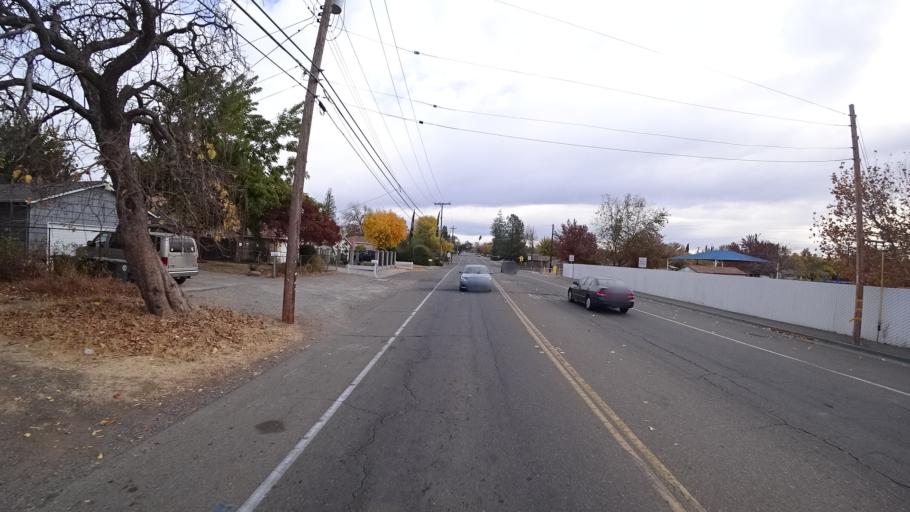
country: US
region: California
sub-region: Sacramento County
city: Citrus Heights
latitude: 38.7003
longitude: -121.2706
